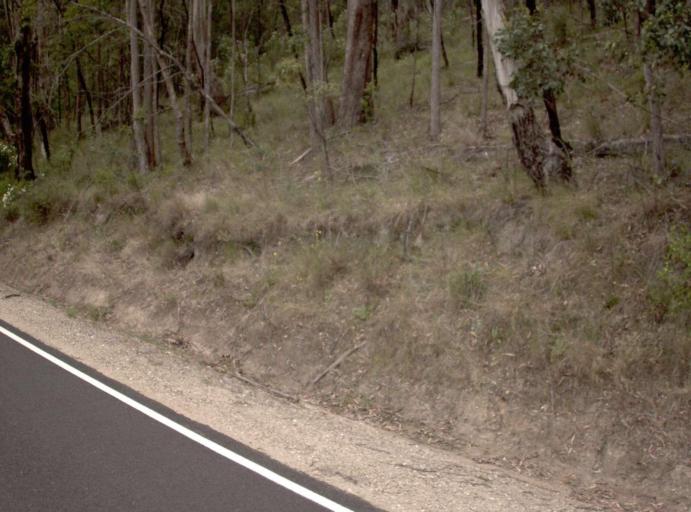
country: AU
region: New South Wales
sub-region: Bombala
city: Bombala
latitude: -37.4485
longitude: 149.1936
